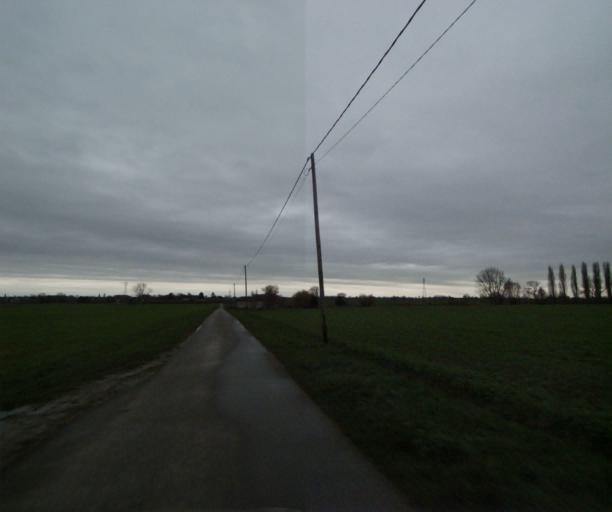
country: FR
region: Nord-Pas-de-Calais
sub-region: Departement du Nord
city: Aubry-du-Hainaut
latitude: 50.3803
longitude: 3.4483
